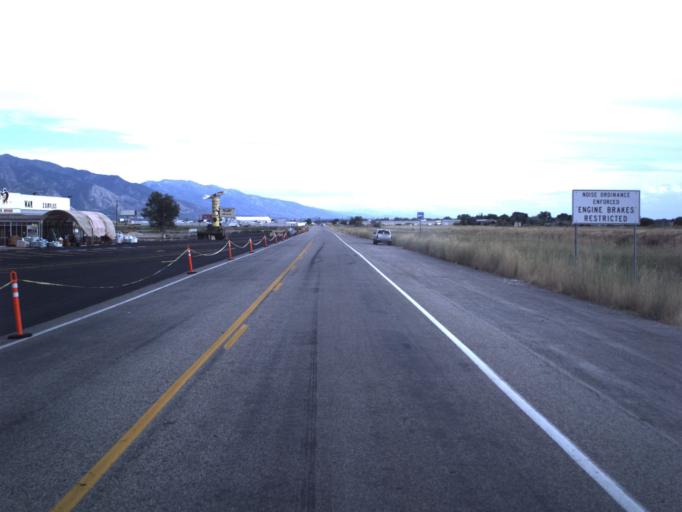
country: US
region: Utah
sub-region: Box Elder County
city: South Willard
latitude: 41.3350
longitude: -112.0369
